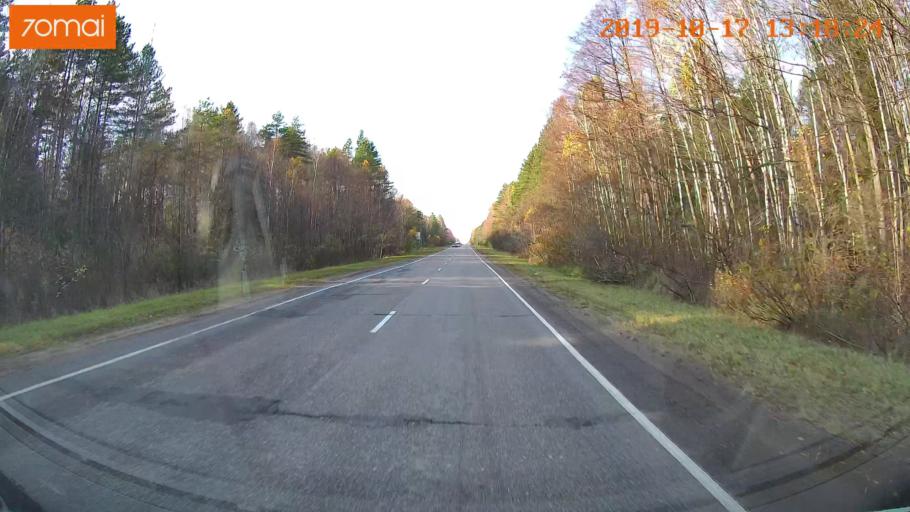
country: RU
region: Rjazan
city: Gus'-Zheleznyy
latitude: 55.0627
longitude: 41.0987
